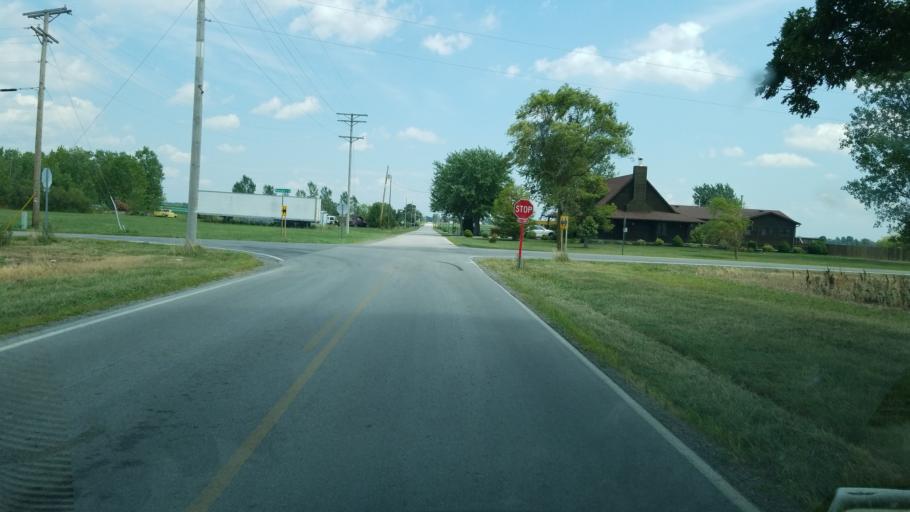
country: US
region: Ohio
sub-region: Hancock County
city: Arlington
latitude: 40.9064
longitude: -83.5962
